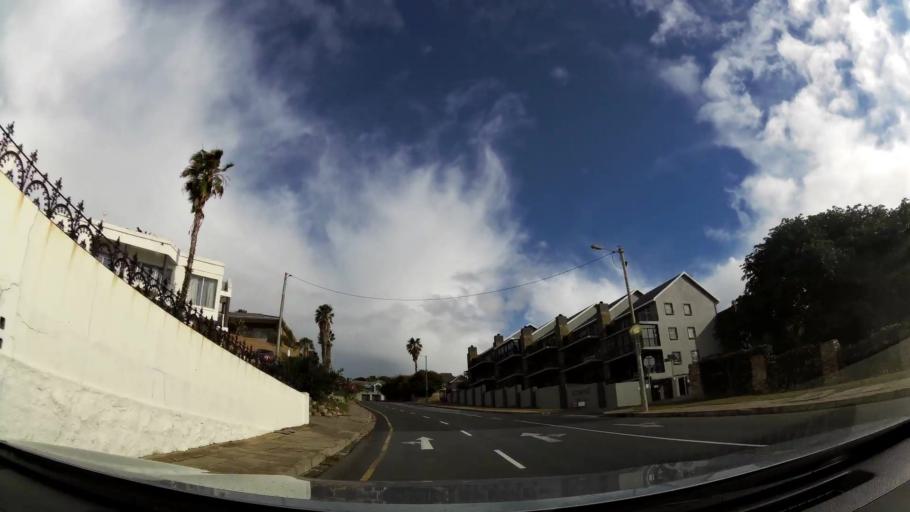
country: ZA
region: Western Cape
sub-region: Eden District Municipality
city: Mossel Bay
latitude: -34.1857
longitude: 22.1403
